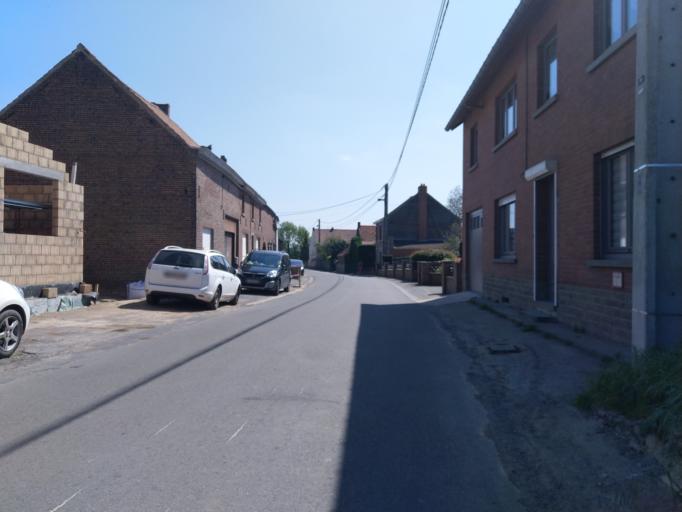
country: BE
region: Wallonia
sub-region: Province du Brabant Wallon
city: Rebecq-Rognon
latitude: 50.6266
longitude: 4.0865
